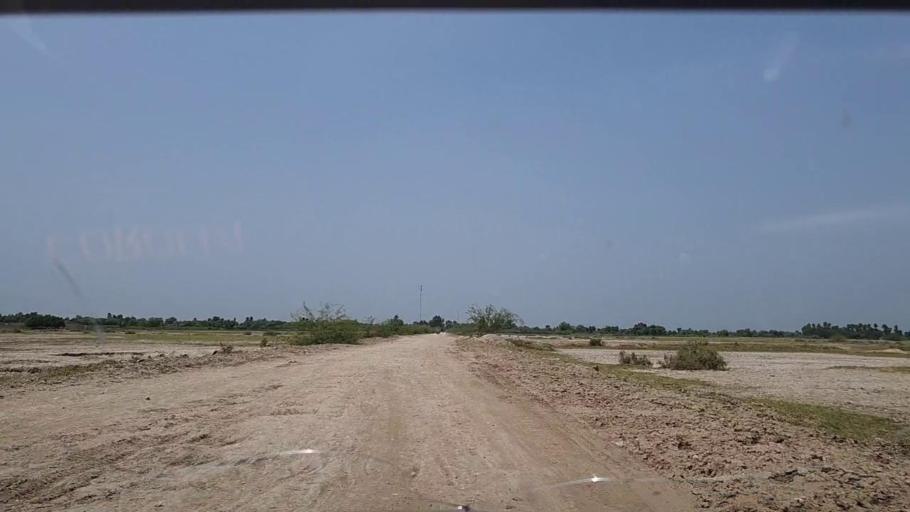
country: PK
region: Sindh
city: Adilpur
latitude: 27.9130
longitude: 69.2120
